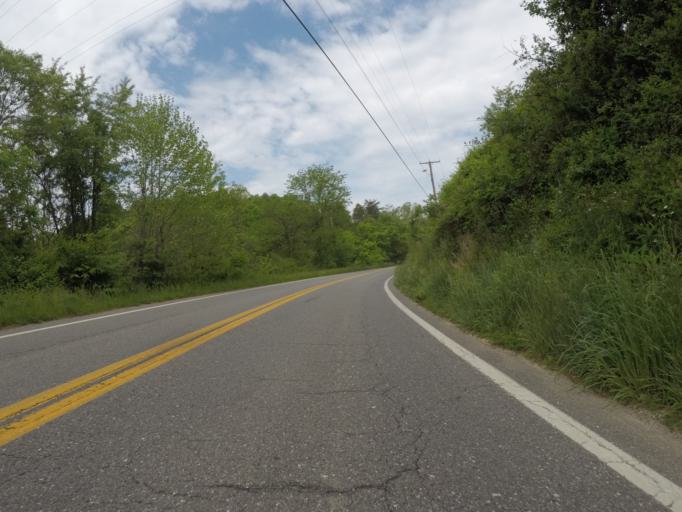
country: US
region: West Virginia
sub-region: Wayne County
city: Ceredo
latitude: 38.3553
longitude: -82.5323
